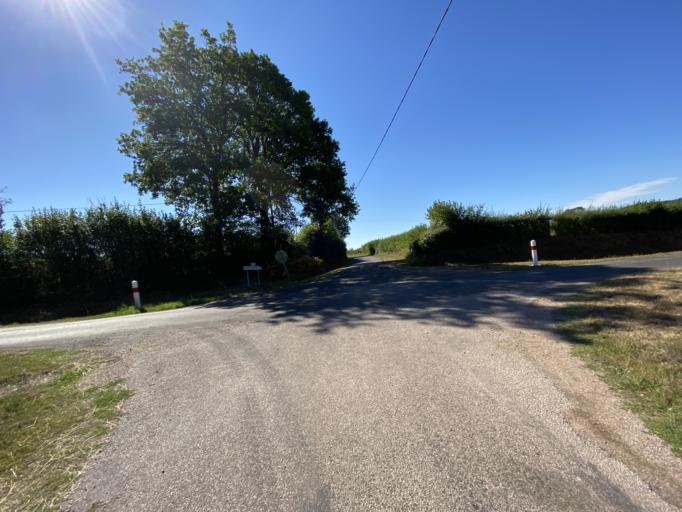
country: FR
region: Bourgogne
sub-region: Departement de la Cote-d'Or
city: Saulieu
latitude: 47.2755
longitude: 4.1788
